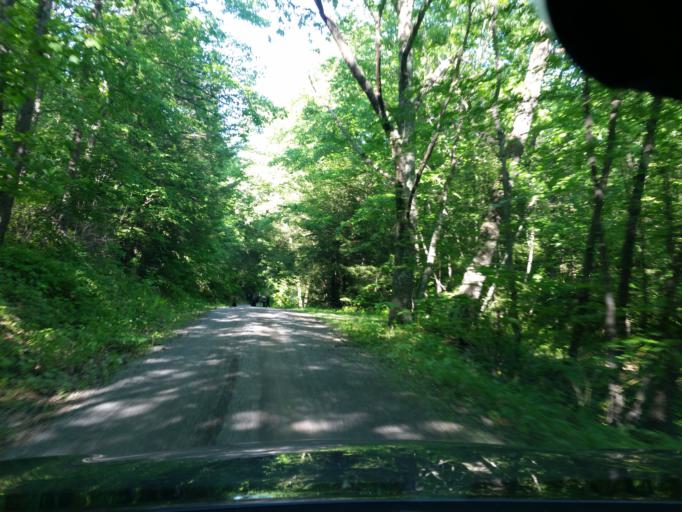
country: US
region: Pennsylvania
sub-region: Lycoming County
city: Jersey Shore
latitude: 41.0901
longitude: -77.1873
